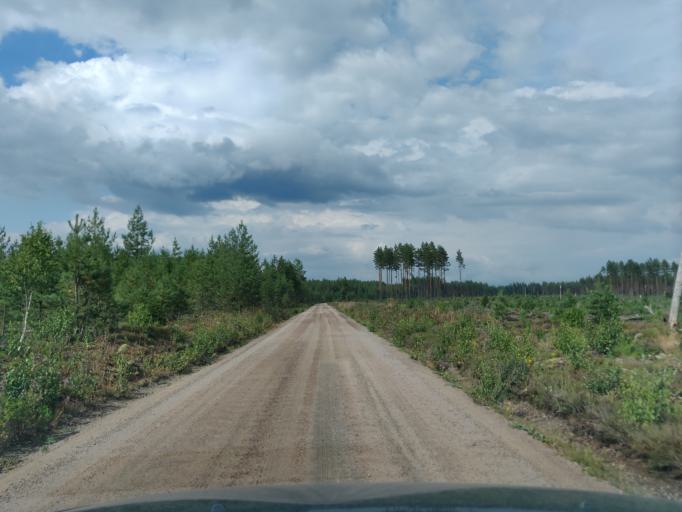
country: SE
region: Vaermland
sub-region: Hagfors Kommun
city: Hagfors
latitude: 59.9760
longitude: 13.5484
